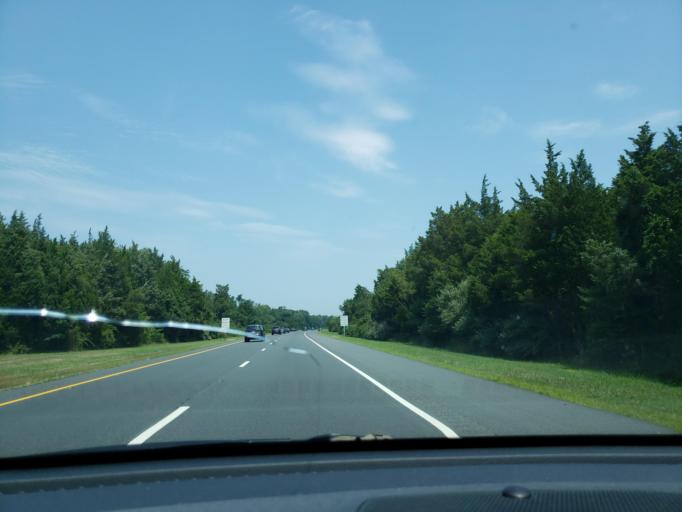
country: US
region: New Jersey
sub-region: Cape May County
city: Sea Isle City
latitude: 39.2070
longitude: -74.6961
